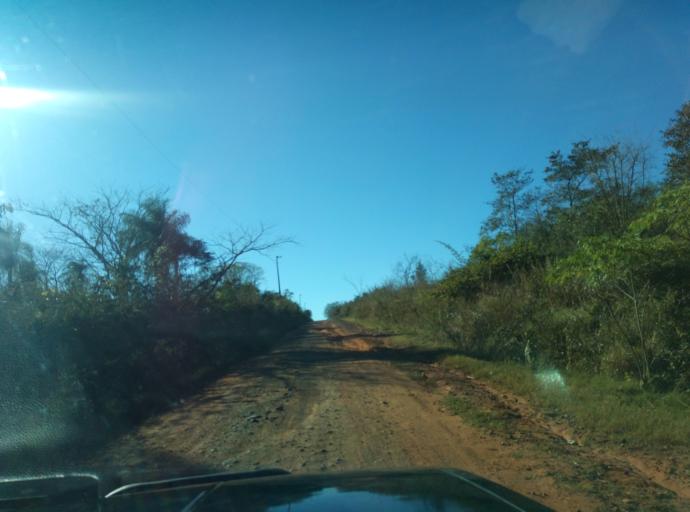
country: PY
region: Caaguazu
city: Carayao
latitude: -25.1579
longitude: -56.2958
